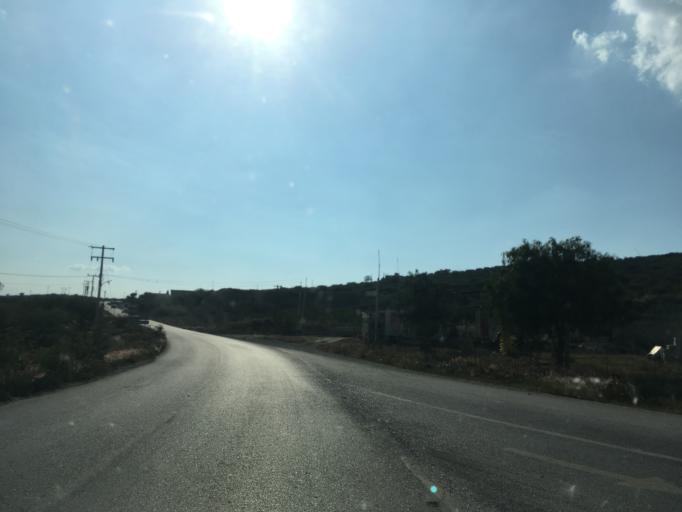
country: MX
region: Hidalgo
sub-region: Ixmiquilpan
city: El Nith
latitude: 20.5737
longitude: -99.1435
